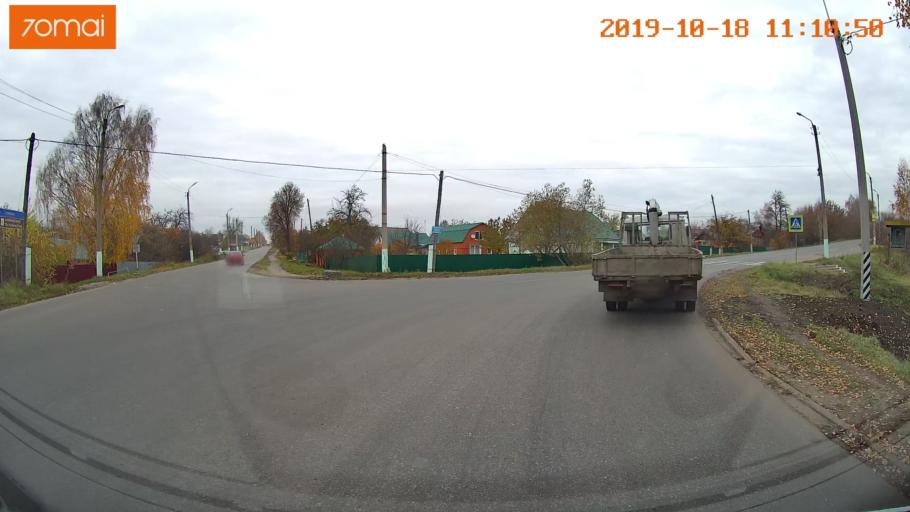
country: RU
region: Tula
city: Kimovsk
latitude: 53.9578
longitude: 38.5383
